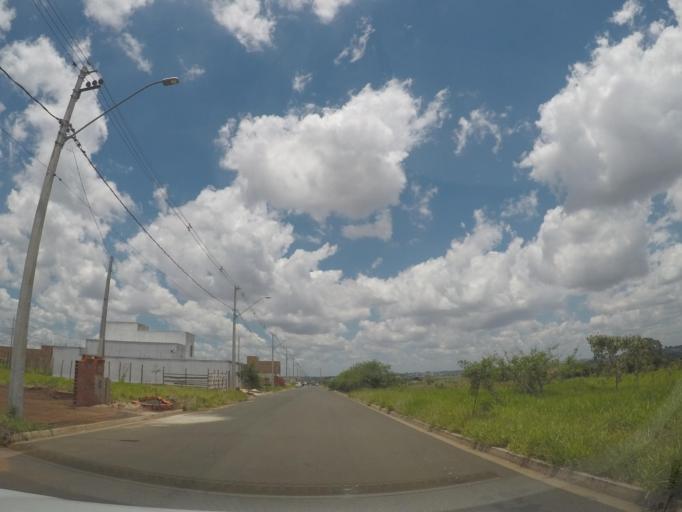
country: BR
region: Sao Paulo
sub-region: Hortolandia
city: Hortolandia
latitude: -22.8380
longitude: -47.2196
